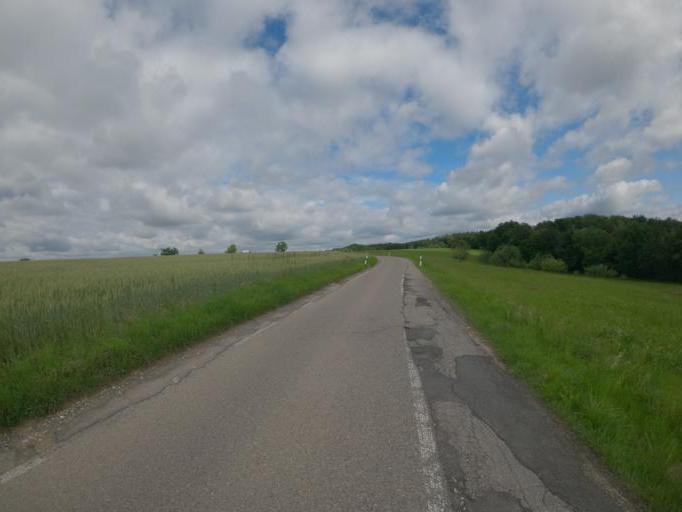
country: DE
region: Baden-Wuerttemberg
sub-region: Regierungsbezirk Stuttgart
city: Ebersbach an der Fils
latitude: 48.7339
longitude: 9.5347
